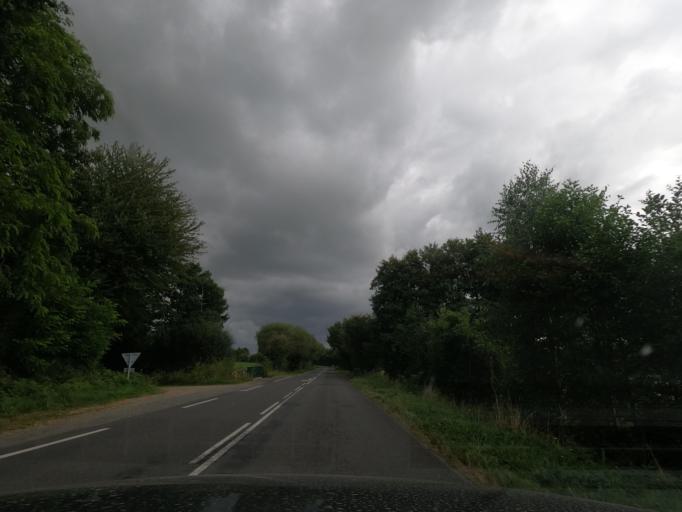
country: FR
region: Lower Normandy
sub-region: Departement de l'Orne
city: Briouze
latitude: 48.6894
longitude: -0.3990
